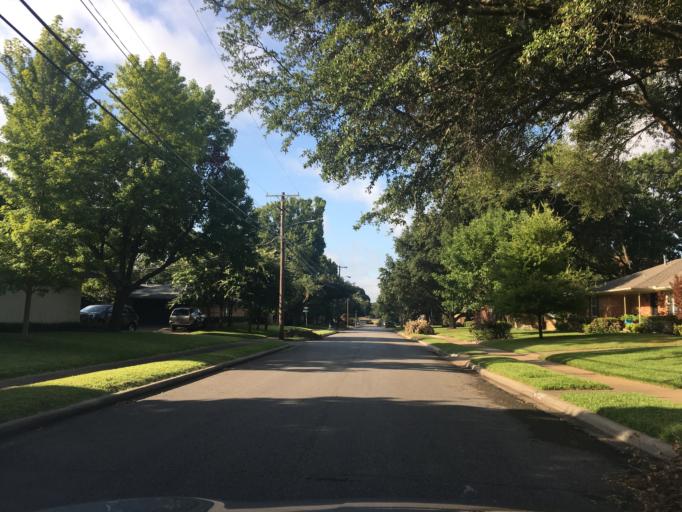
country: US
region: Texas
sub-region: Dallas County
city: Highland Park
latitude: 32.8457
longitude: -96.7607
